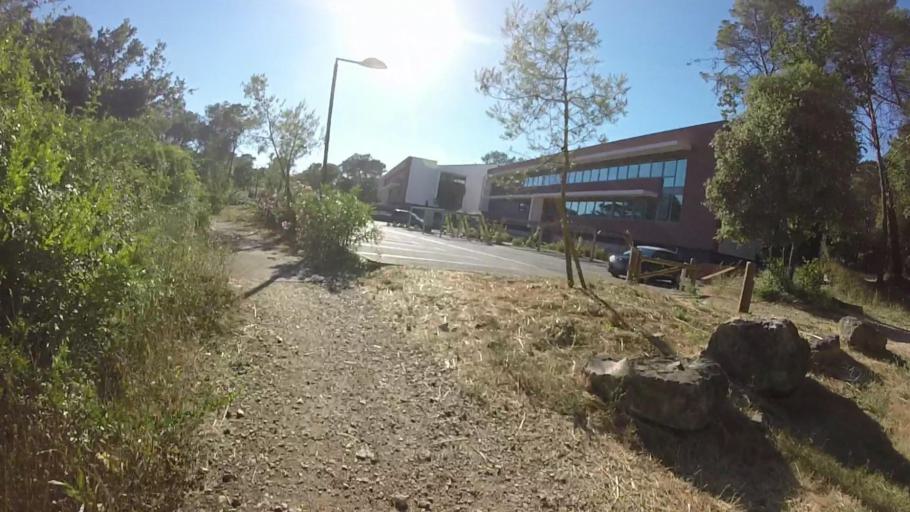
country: FR
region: Provence-Alpes-Cote d'Azur
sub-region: Departement des Alpes-Maritimes
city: Mougins
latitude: 43.6092
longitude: 7.0234
